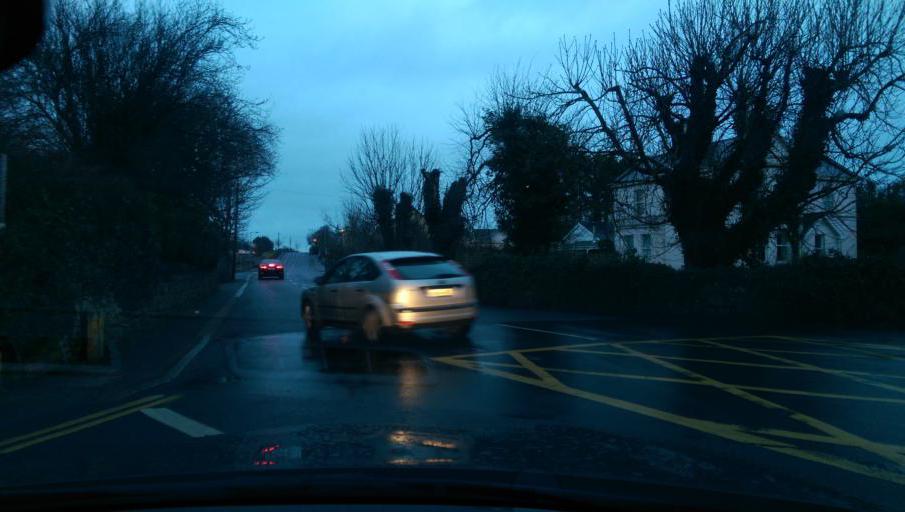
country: IE
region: Connaught
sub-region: County Galway
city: Athenry
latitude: 53.3026
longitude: -8.7488
